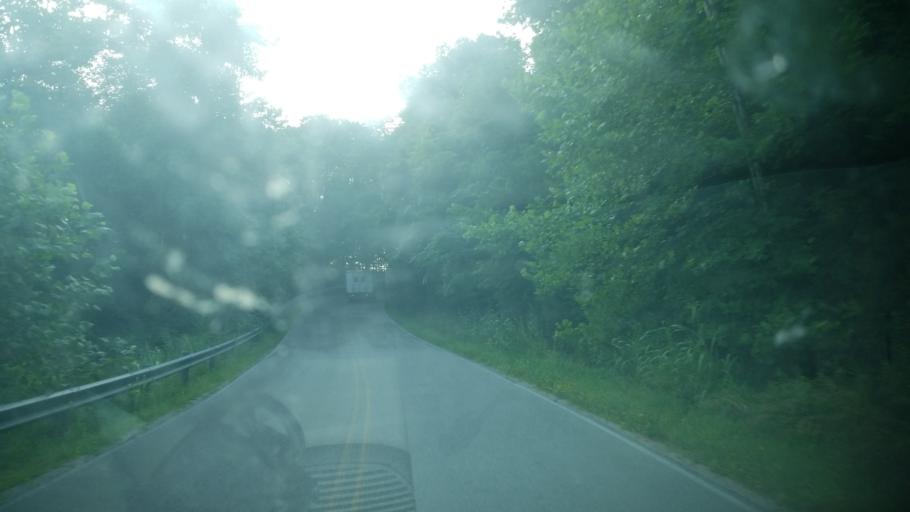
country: US
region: Ohio
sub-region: Adams County
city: West Union
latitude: 38.8600
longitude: -83.4783
